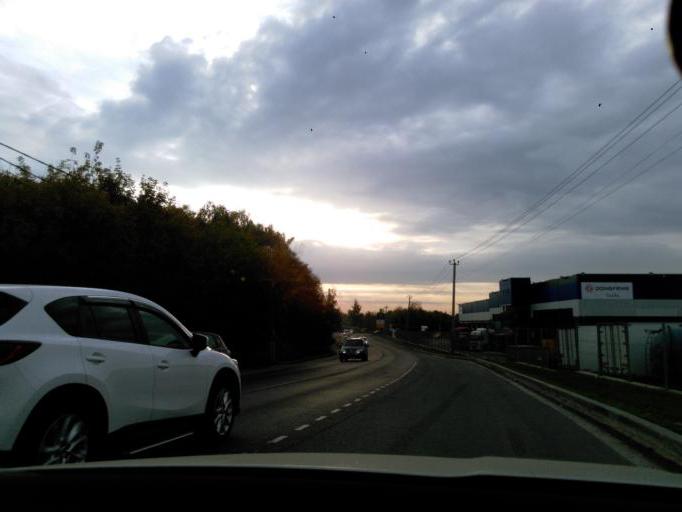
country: RU
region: Moskovskaya
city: Sheremet'yevskiy
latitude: 55.9717
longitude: 37.4700
